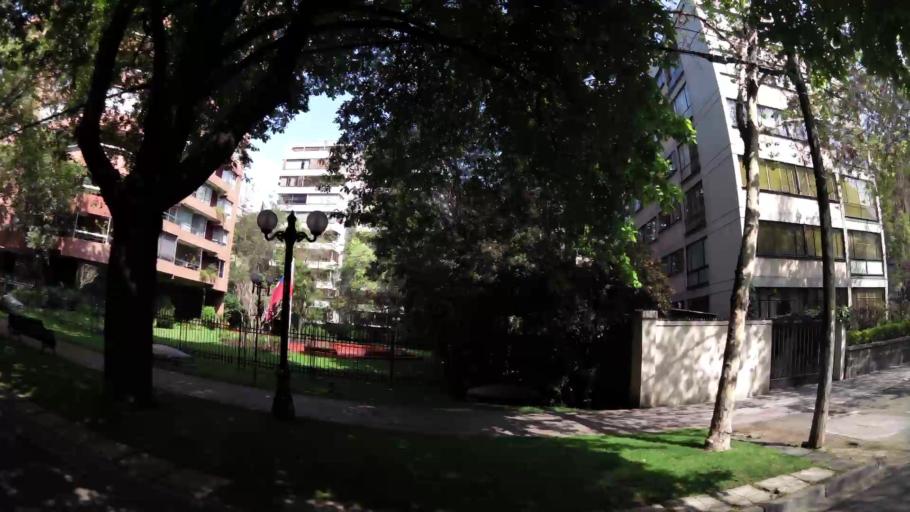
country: CL
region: Santiago Metropolitan
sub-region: Provincia de Santiago
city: Villa Presidente Frei, Nunoa, Santiago, Chile
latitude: -33.4229
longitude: -70.6000
